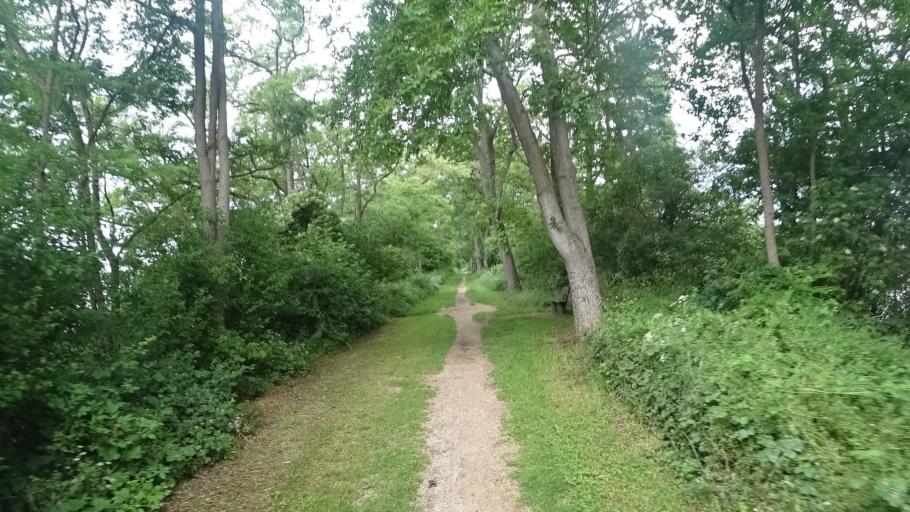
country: DE
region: Rheinland-Pfalz
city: Bad Neuenahr-Ahrweiler
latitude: 50.5690
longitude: 7.0971
